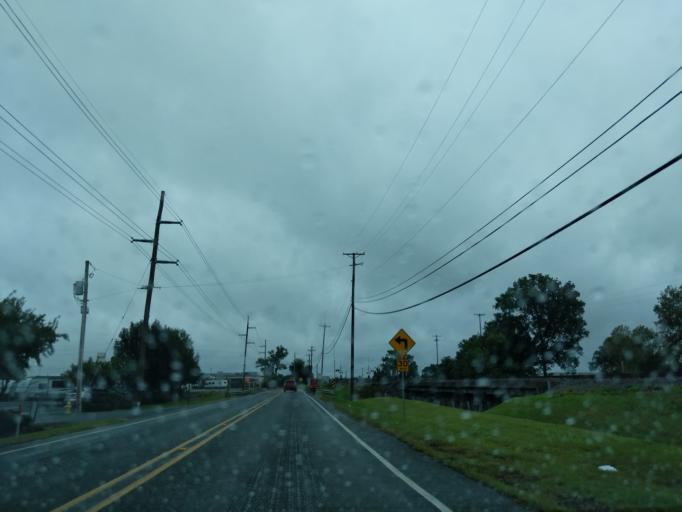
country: US
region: Louisiana
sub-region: Bossier Parish
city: Bossier City
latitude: 32.5263
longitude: -93.6773
